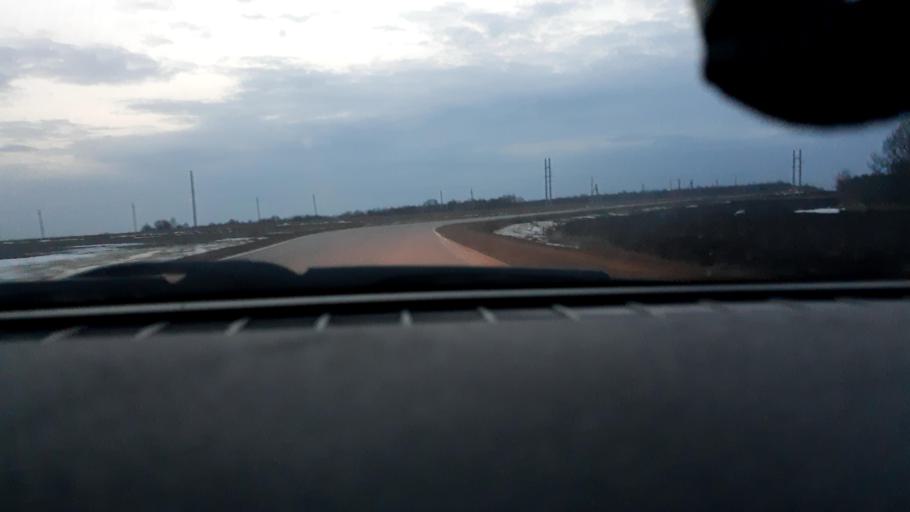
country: RU
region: Bashkortostan
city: Ulukulevo
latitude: 54.5292
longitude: 56.3796
